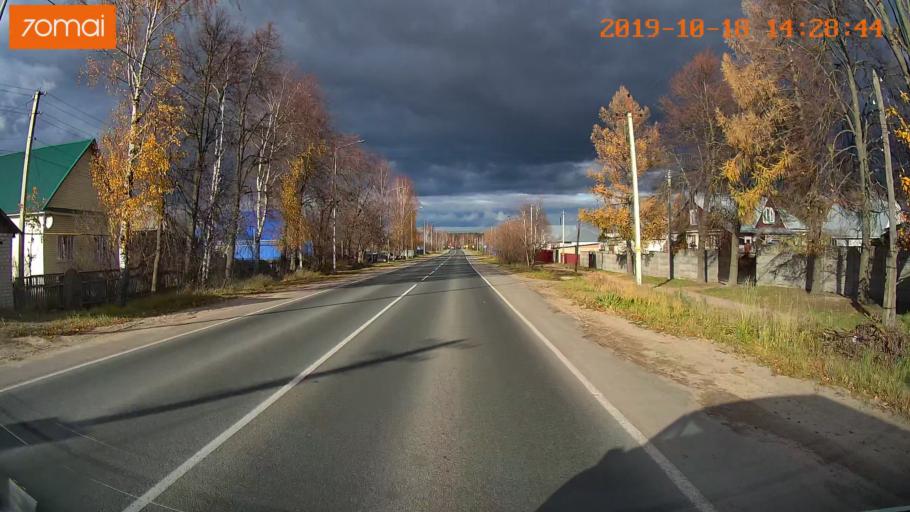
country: RU
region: Rjazan
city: Tuma
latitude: 55.1504
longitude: 40.5547
